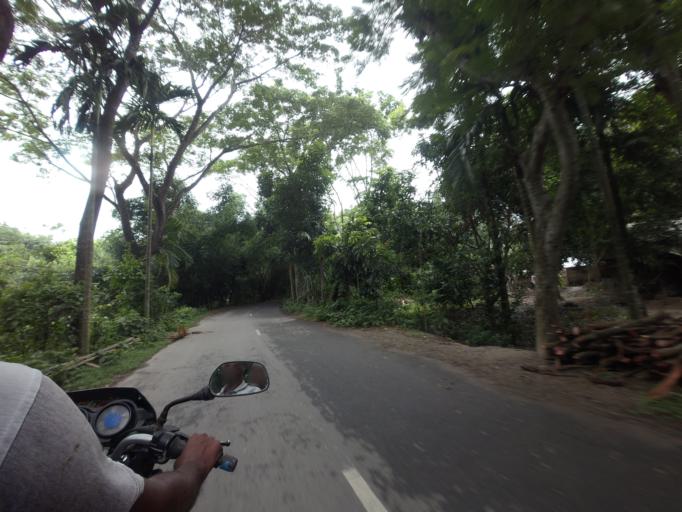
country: BD
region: Khulna
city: Kalia
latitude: 23.1323
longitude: 89.6414
